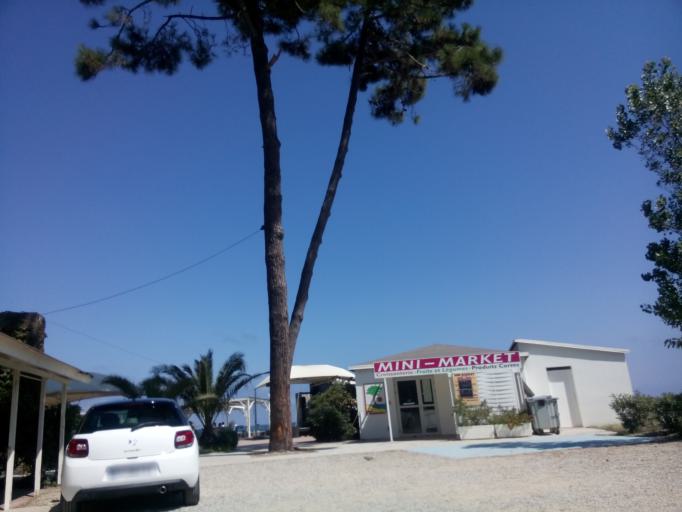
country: FR
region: Corsica
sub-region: Departement de la Haute-Corse
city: Aleria
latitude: 42.1103
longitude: 9.5505
